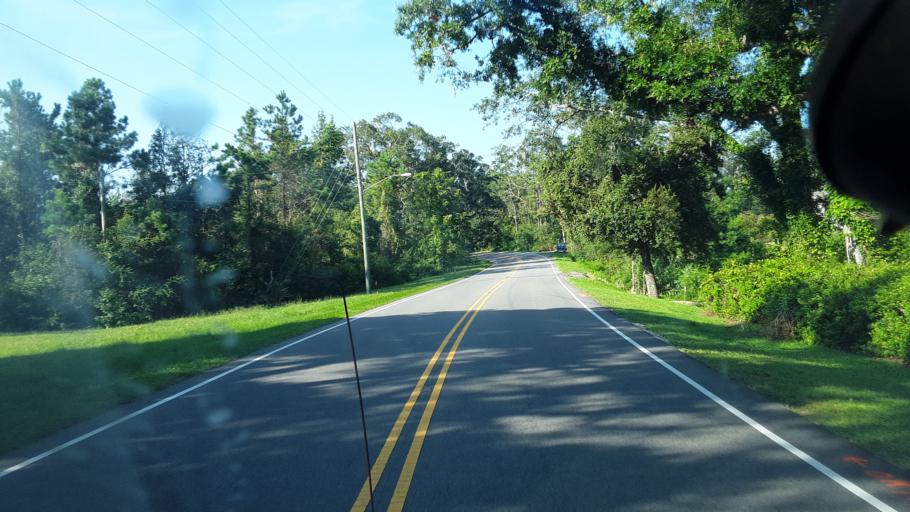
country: US
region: North Carolina
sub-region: Brunswick County
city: Belville
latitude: 34.2157
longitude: -77.9822
